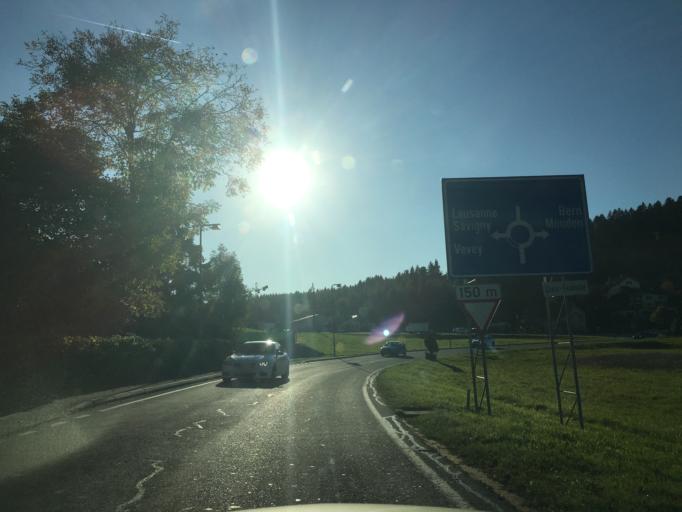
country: CH
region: Vaud
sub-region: Lavaux-Oron District
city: Oron-la-ville
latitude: 46.5594
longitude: 6.7845
